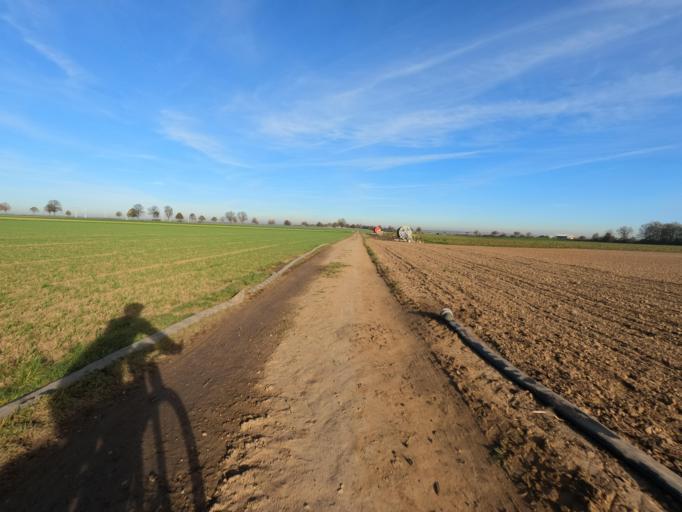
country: DE
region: North Rhine-Westphalia
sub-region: Regierungsbezirk Koln
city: Titz
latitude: 51.0441
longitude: 6.4255
